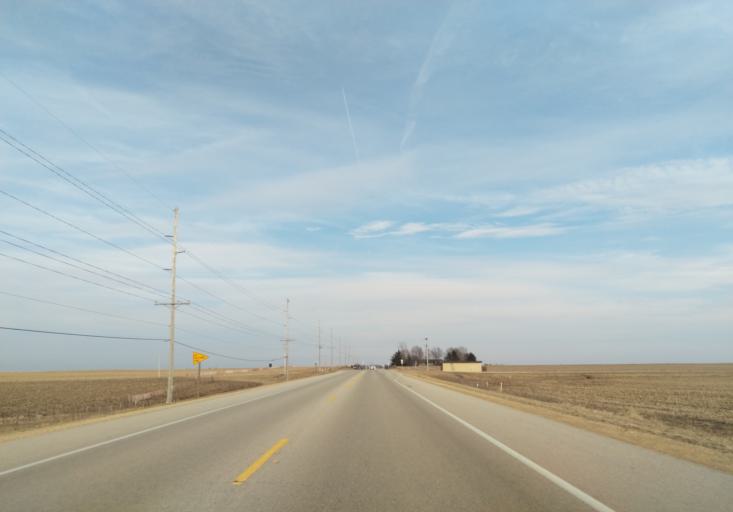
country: US
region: Wisconsin
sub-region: Iowa County
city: Mineral Point
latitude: 42.9676
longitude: -90.3125
